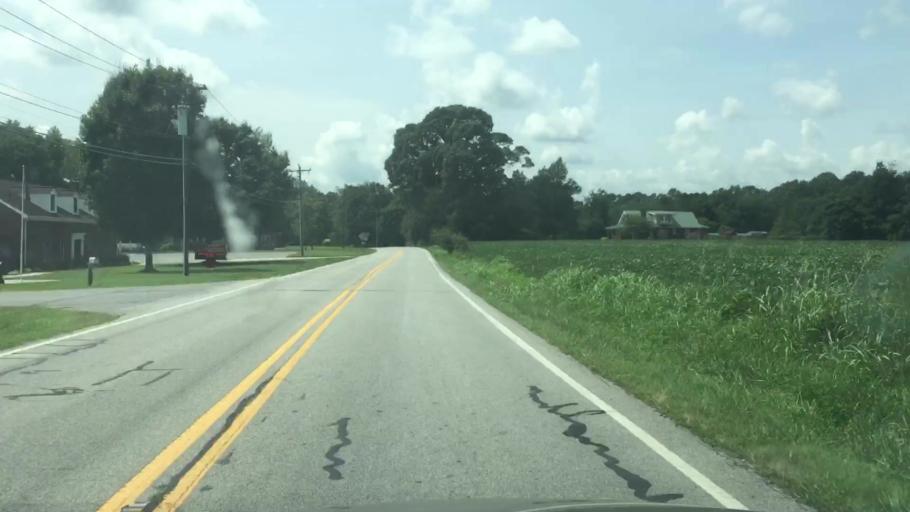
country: US
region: North Carolina
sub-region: Rowan County
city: China Grove
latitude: 35.6529
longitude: -80.5887
